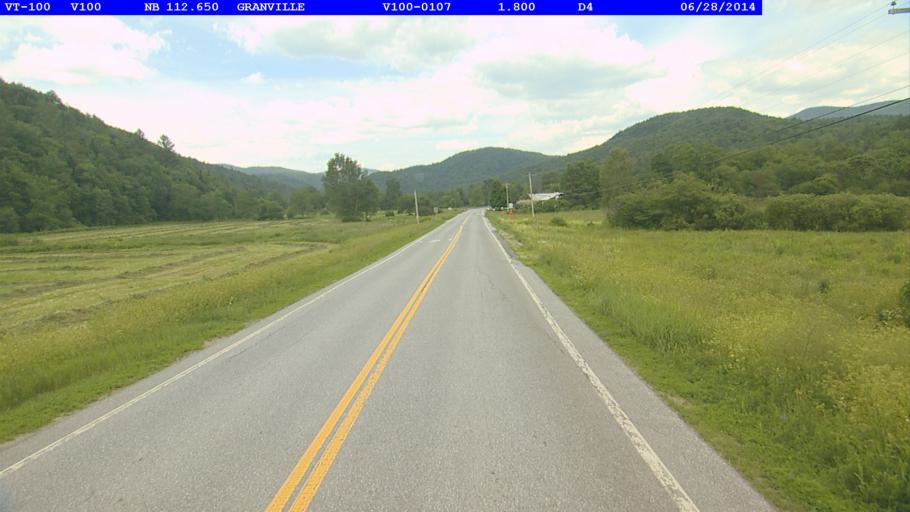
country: US
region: Vermont
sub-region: Orange County
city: Randolph
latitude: 43.9703
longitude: -72.8432
